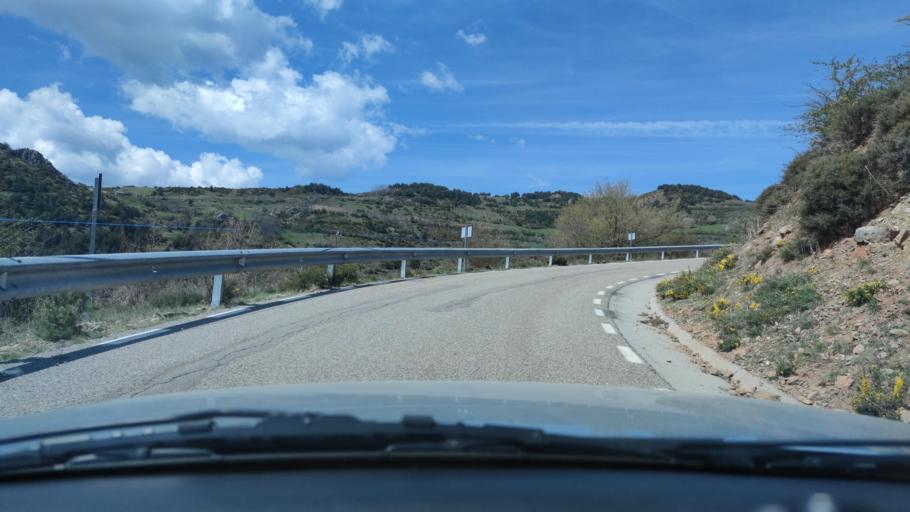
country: ES
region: Catalonia
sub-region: Provincia de Lleida
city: Coll de Nargo
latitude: 42.2919
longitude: 1.2424
